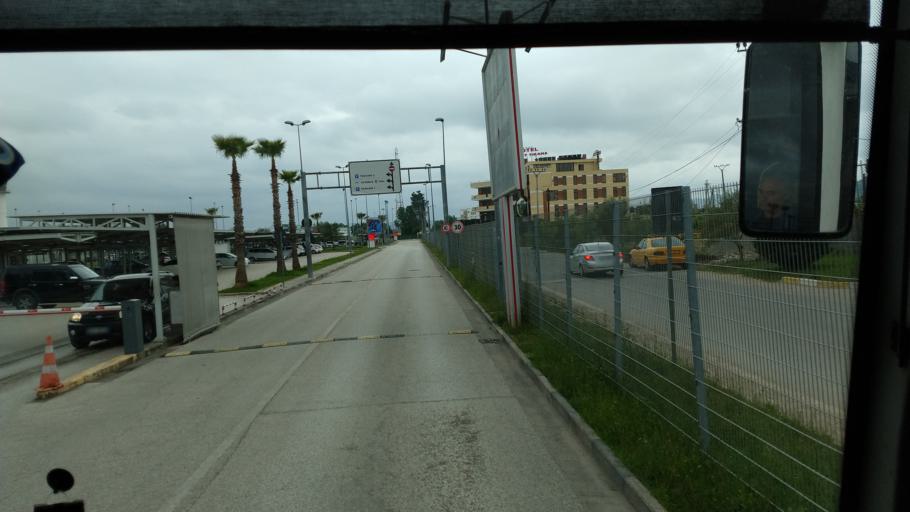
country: AL
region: Tirane
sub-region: Rrethi i Tiranes
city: Preze
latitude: 41.4182
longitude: 19.7127
